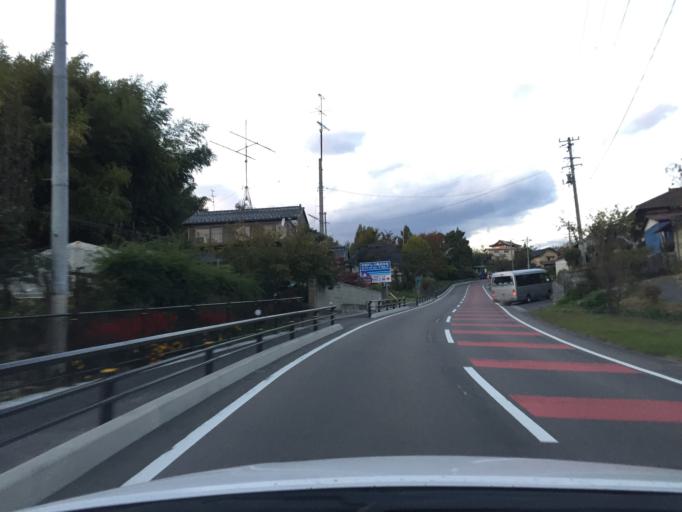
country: JP
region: Fukushima
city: Miharu
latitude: 37.4571
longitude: 140.4391
